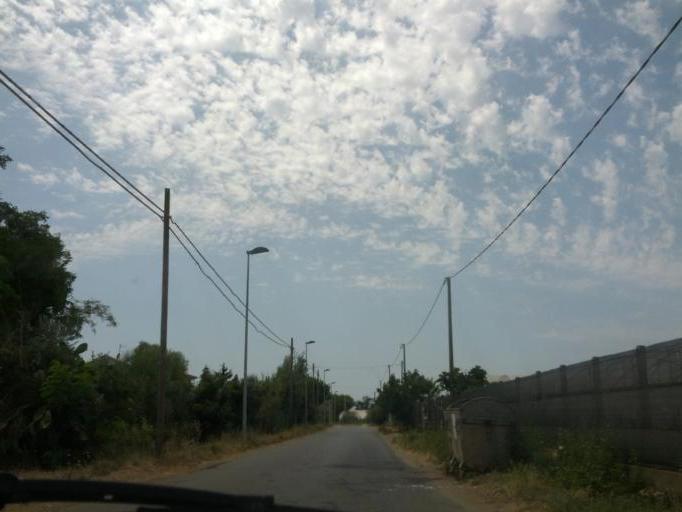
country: IT
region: Latium
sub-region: Provincia di Latina
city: Sperlonga
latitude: 41.2914
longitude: 13.3948
